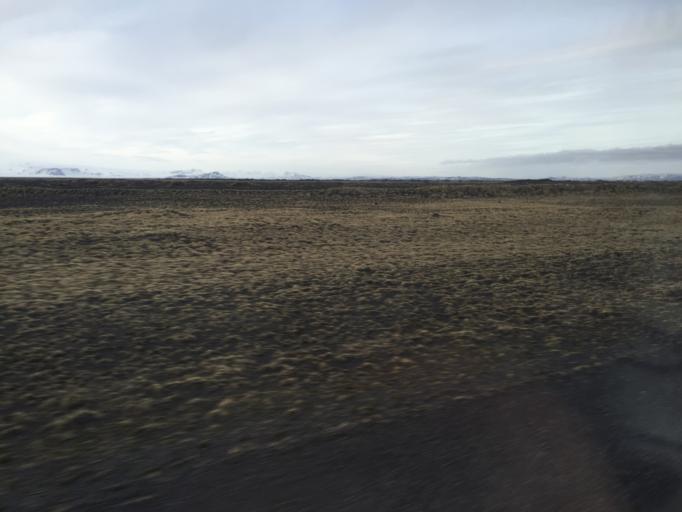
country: IS
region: South
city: Vestmannaeyjar
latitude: 63.5051
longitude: -18.4984
